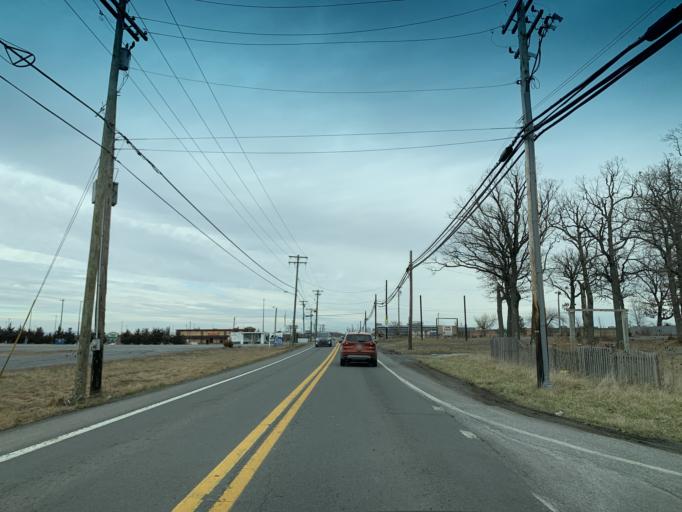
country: US
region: West Virginia
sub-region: Berkeley County
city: Martinsburg
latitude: 39.5399
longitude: -77.9086
